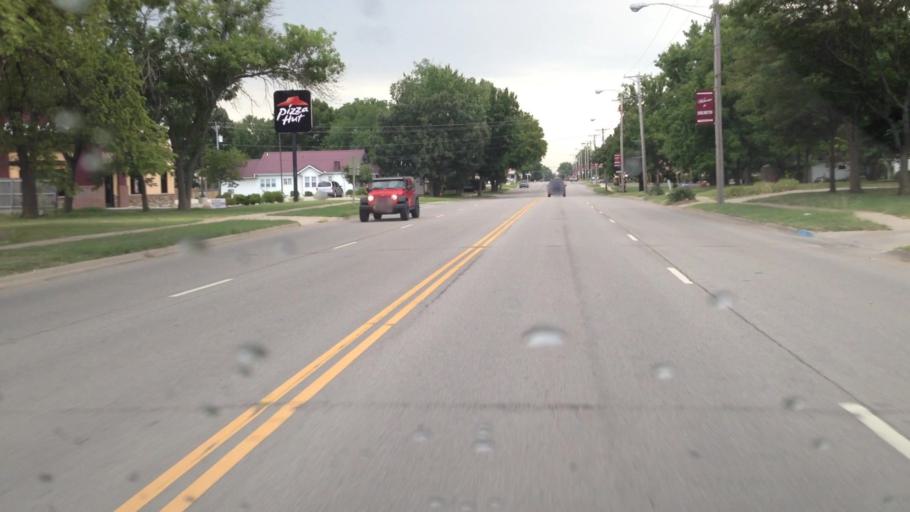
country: US
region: Kansas
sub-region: Coffey County
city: Burlington
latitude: 38.2015
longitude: -95.7386
